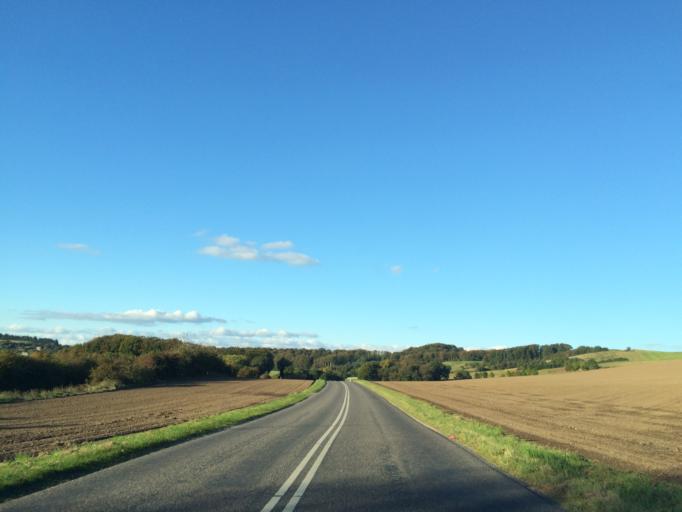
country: DK
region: Central Jutland
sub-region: Skanderborg Kommune
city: Ry
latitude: 56.1147
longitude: 9.7341
